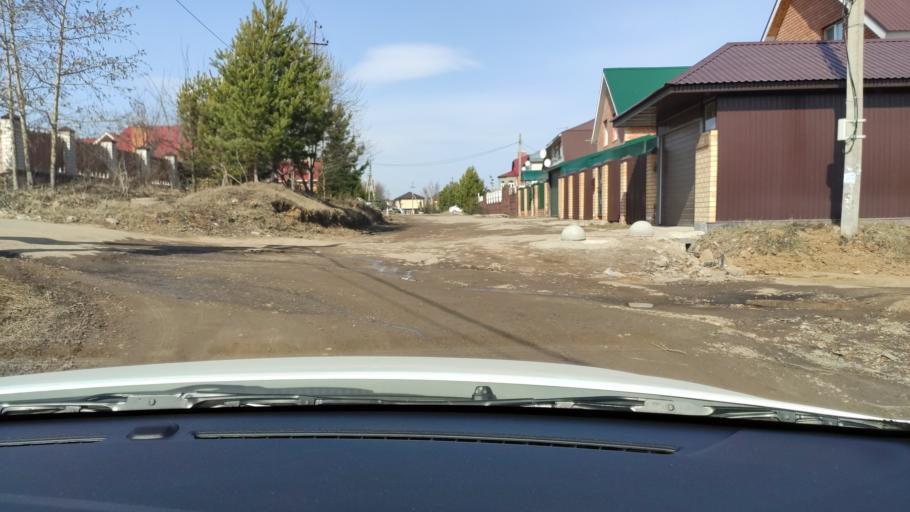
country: RU
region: Tatarstan
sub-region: Gorod Kazan'
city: Kazan
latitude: 55.7852
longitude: 49.2479
